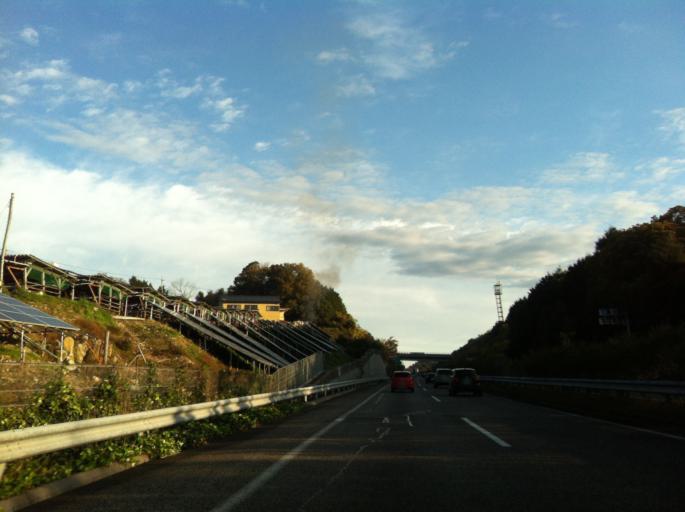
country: JP
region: Aichi
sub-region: Toyota-shi
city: Toyota
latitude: 35.0793
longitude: 137.2142
